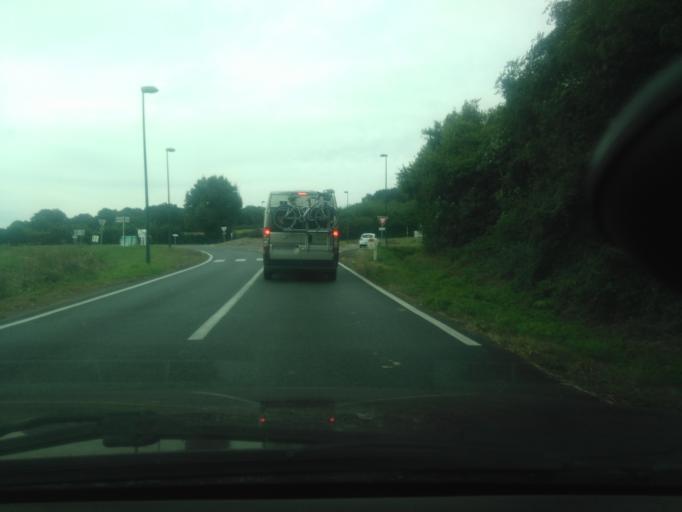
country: FR
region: Pays de la Loire
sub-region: Departement de la Vendee
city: Mouilleron-en-Pareds
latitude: 46.6776
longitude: -0.8403
